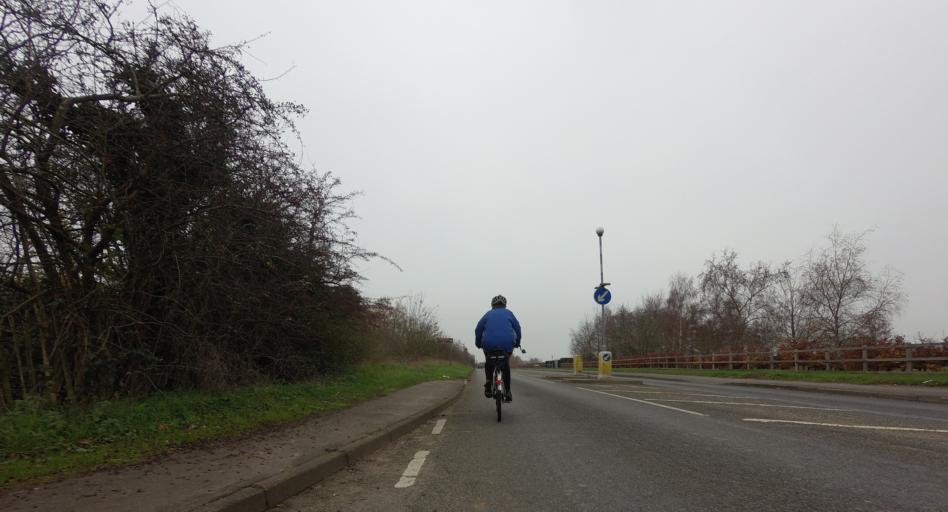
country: GB
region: England
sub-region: Kent
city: Swanley
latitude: 51.4134
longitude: 0.1656
